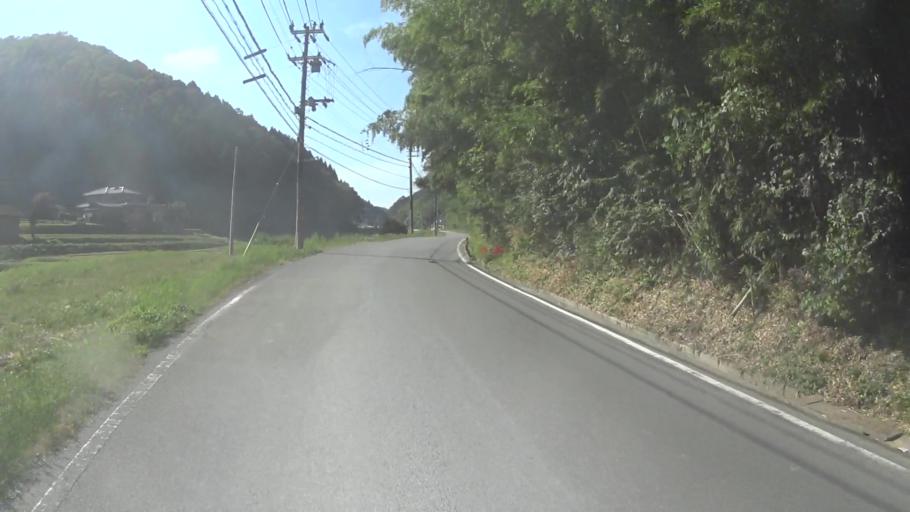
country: JP
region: Kyoto
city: Kameoka
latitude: 34.9484
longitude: 135.5469
